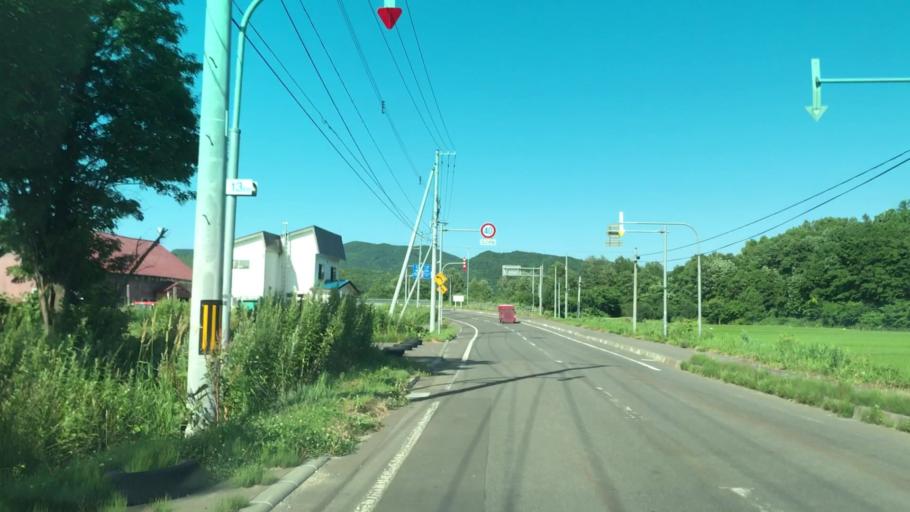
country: JP
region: Hokkaido
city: Yoichi
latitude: 43.0486
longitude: 140.8226
